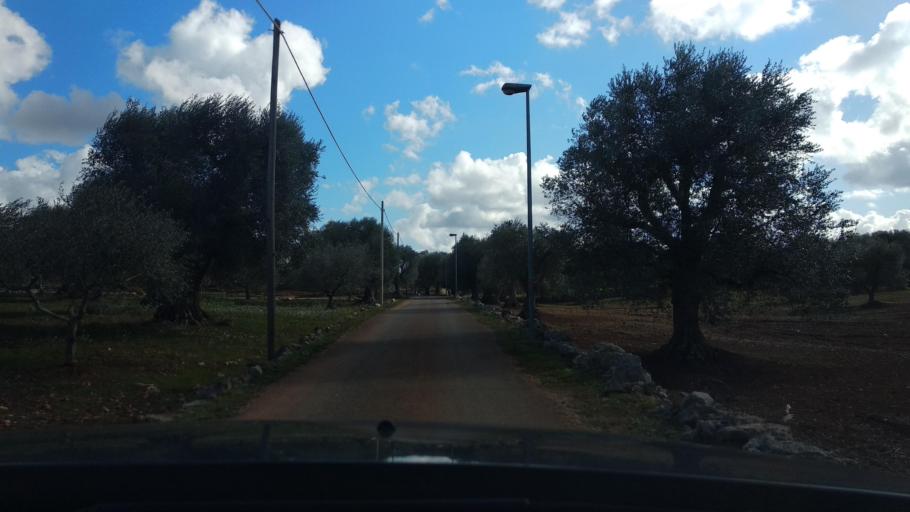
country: IT
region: Apulia
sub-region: Provincia di Brindisi
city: Casalini
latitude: 40.6959
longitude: 17.4834
